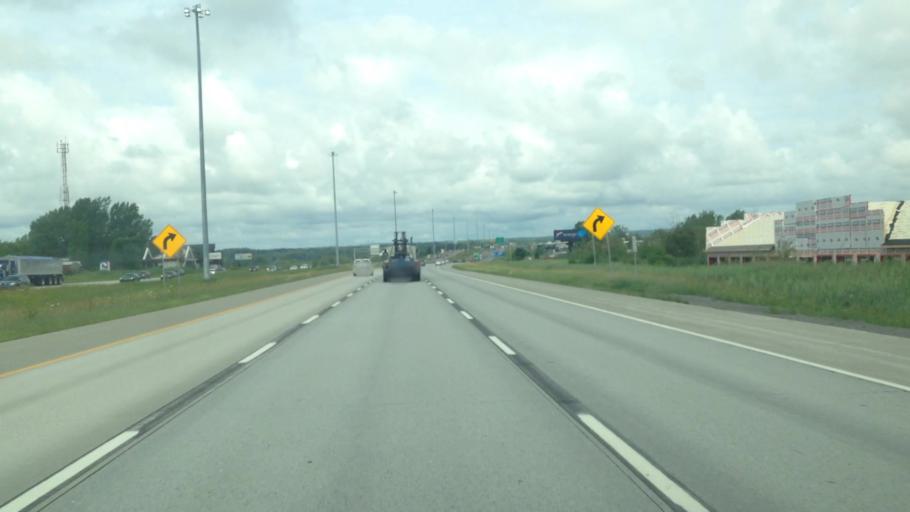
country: CA
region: Quebec
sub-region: Laurentides
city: Saint-Jerome
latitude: 45.7391
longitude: -73.9923
